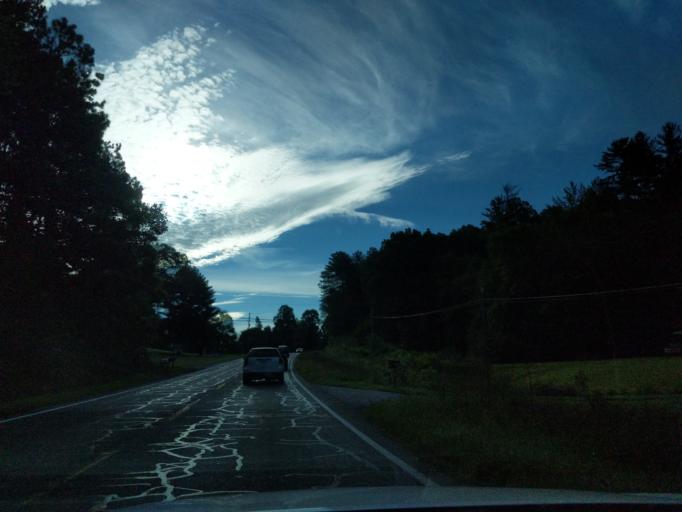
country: US
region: Georgia
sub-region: Fannin County
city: Blue Ridge
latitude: 34.8858
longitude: -84.3359
